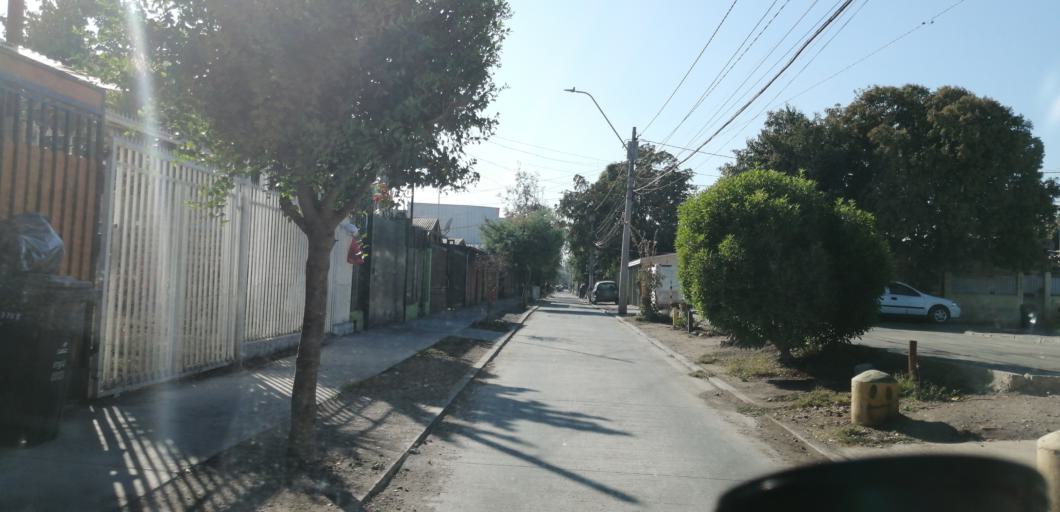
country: CL
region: Santiago Metropolitan
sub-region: Provincia de Santiago
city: Lo Prado
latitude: -33.4307
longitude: -70.7532
